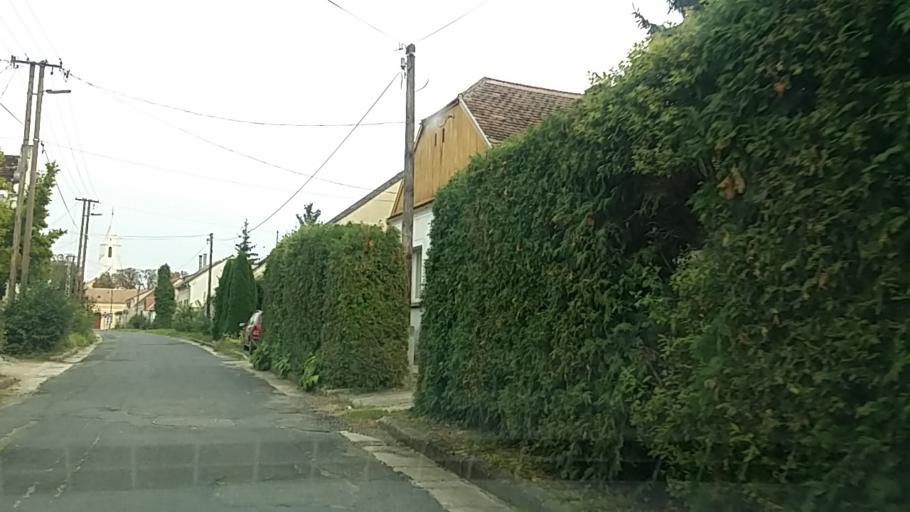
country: HU
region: Vas
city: Csepreg
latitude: 47.4017
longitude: 16.7042
